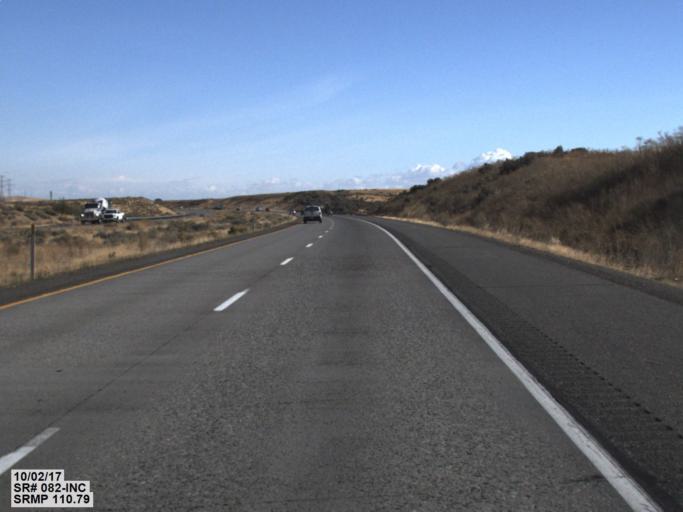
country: US
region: Washington
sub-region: Franklin County
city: West Pasco
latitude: 46.1789
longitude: -119.2374
